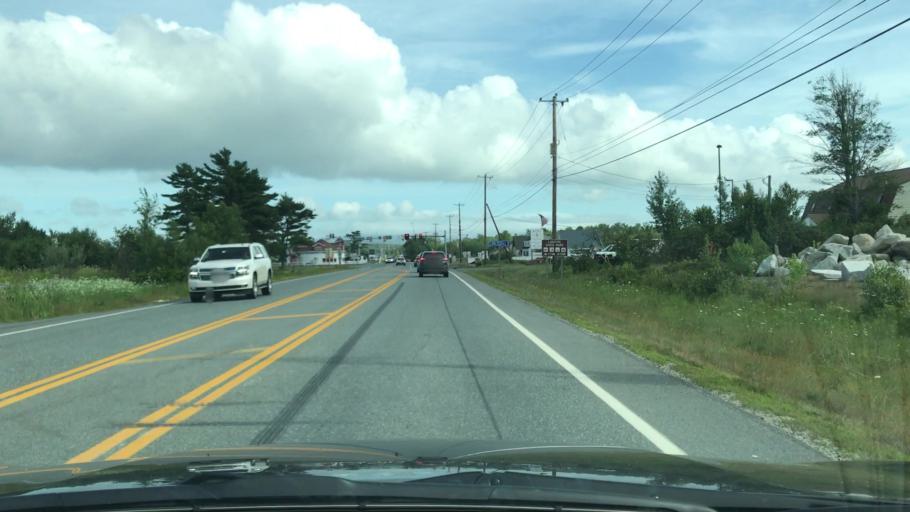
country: US
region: Maine
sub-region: Hancock County
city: Trenton
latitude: 44.4899
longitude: -68.3723
